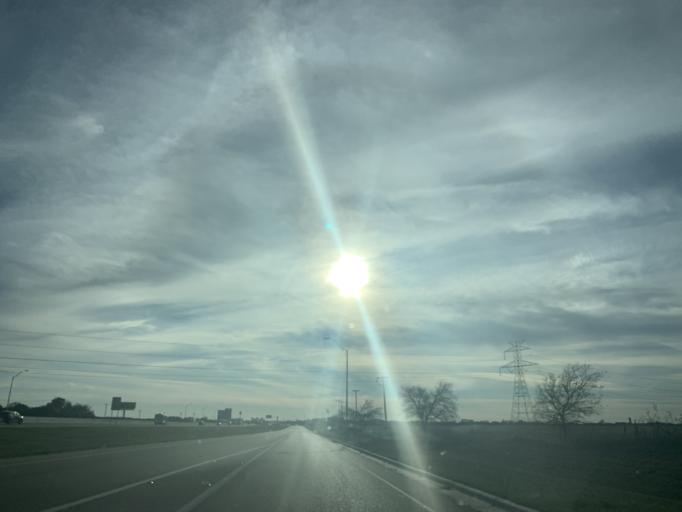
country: US
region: Texas
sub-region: Bell County
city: Salado
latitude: 30.9743
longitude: -97.5166
